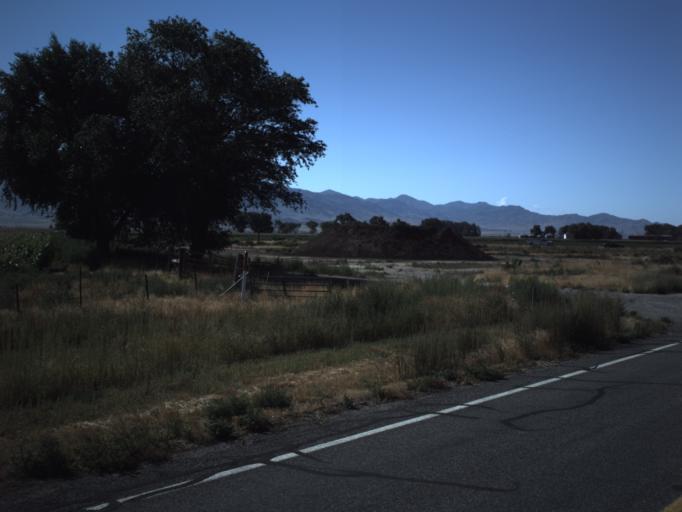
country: US
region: Utah
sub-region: Millard County
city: Delta
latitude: 39.5266
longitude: -112.3719
